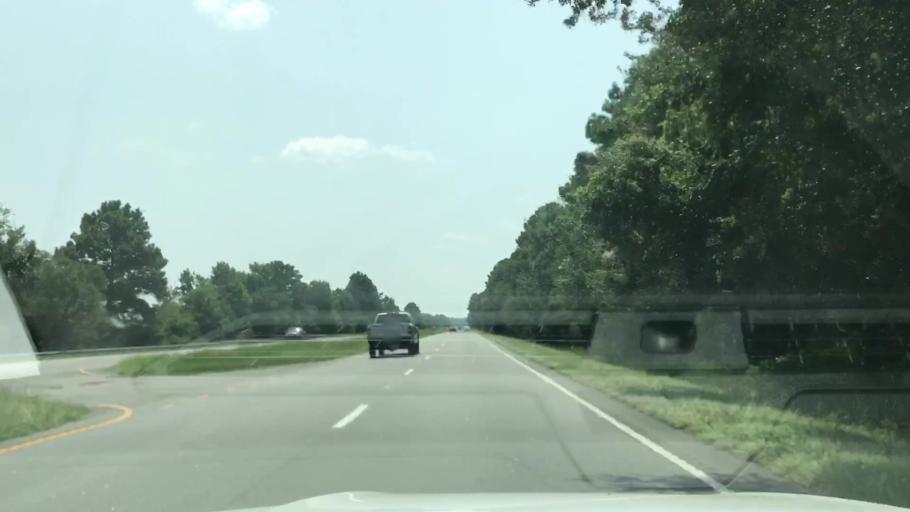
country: US
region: South Carolina
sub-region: Georgetown County
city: Georgetown
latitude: 33.2001
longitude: -79.3921
